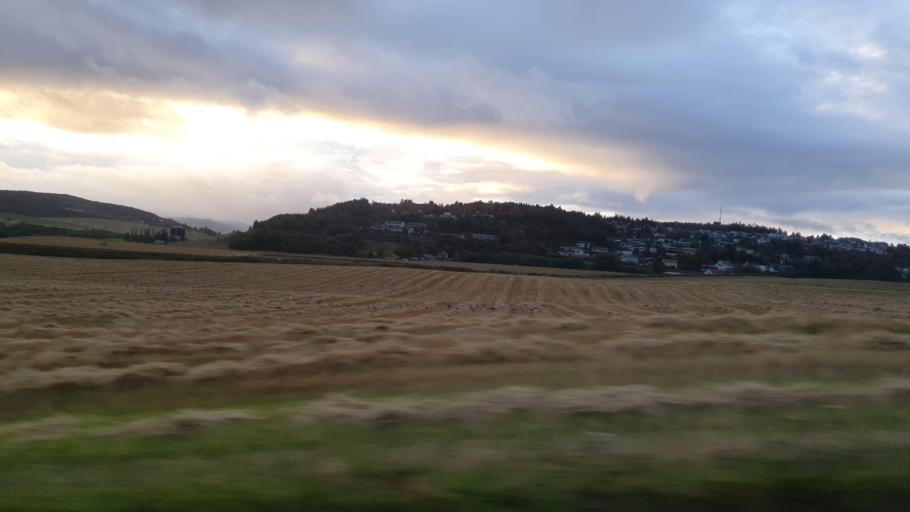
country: NO
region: Nord-Trondelag
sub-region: Levanger
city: Skogn
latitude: 63.6922
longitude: 11.1917
